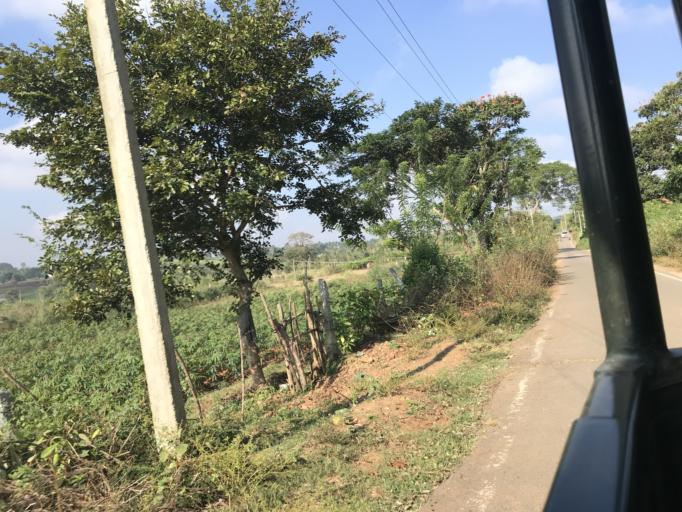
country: IN
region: Karnataka
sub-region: Mysore
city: Heggadadevankote
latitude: 11.9458
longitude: 76.2648
